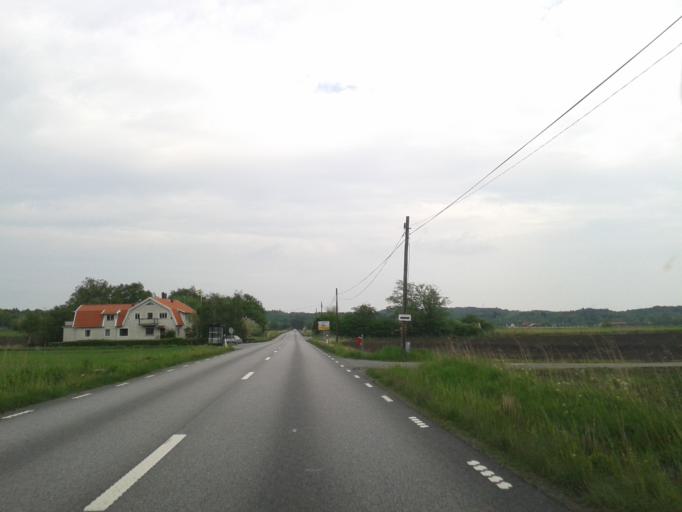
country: SE
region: Vaestra Goetaland
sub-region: Kungalvs Kommun
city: Kode
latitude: 57.8917
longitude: 11.7864
